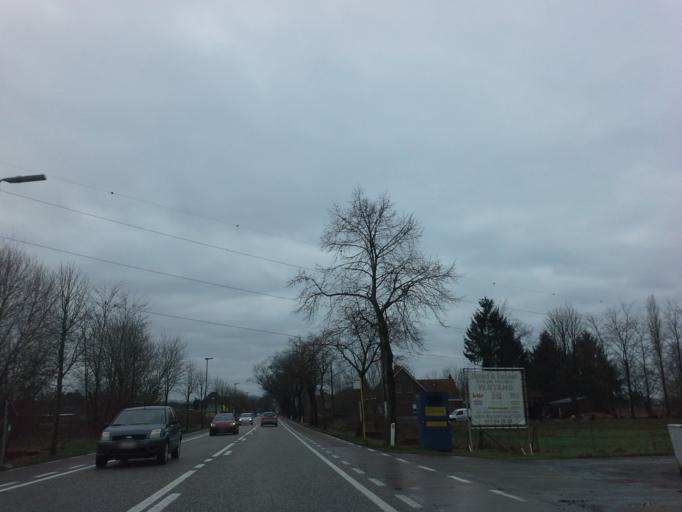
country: BE
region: Flanders
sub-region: Provincie Limburg
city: Leopoldsburg
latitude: 51.1582
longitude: 5.2613
